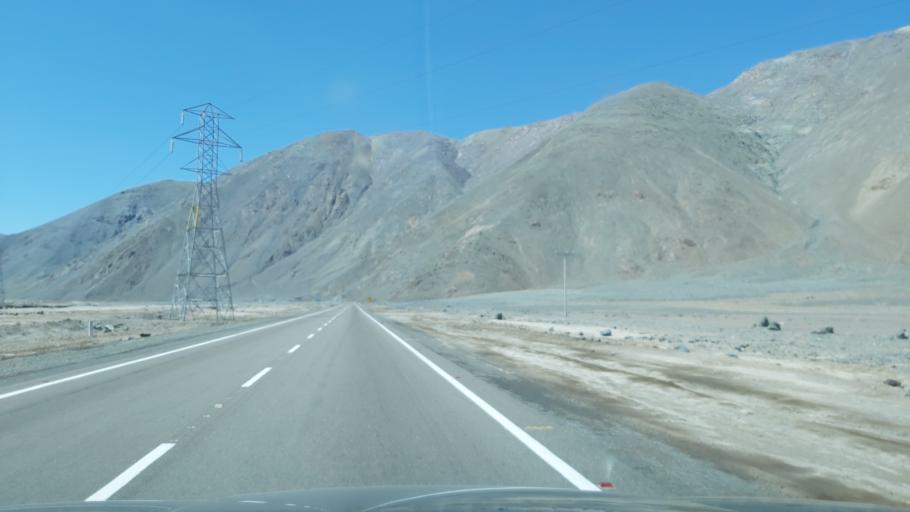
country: CL
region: Atacama
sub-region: Provincia de Chanaral
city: Diego de Almagro
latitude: -26.3445
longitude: -69.7437
